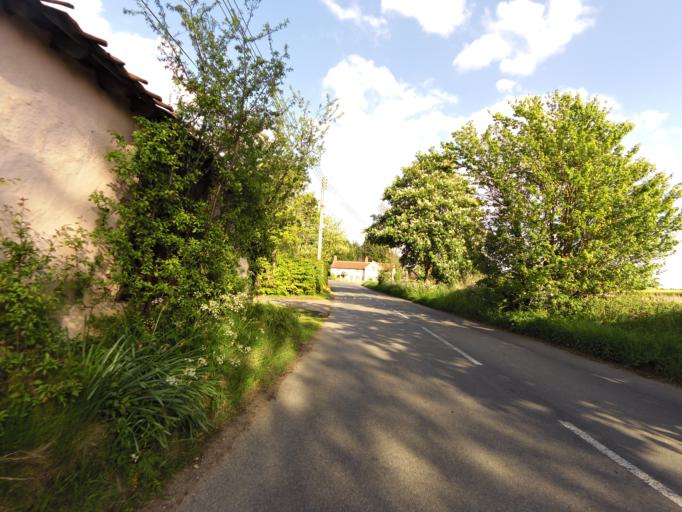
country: GB
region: England
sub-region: Suffolk
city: Beccles
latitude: 52.4036
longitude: 1.5392
